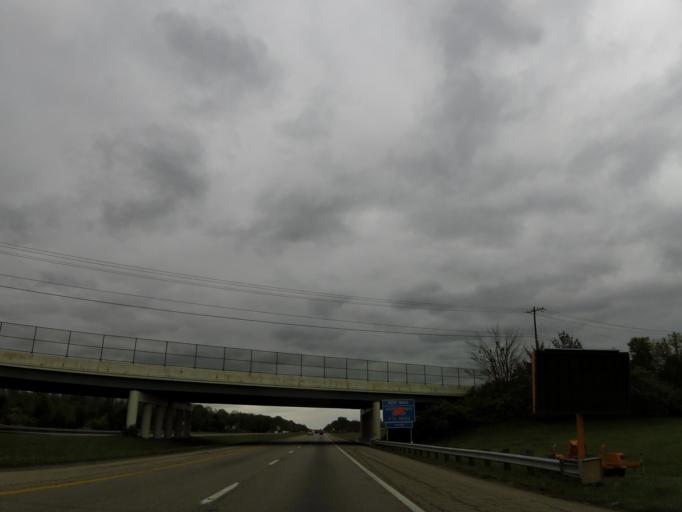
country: US
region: Ohio
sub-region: Warren County
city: Lebanon
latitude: 39.4127
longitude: -84.1536
